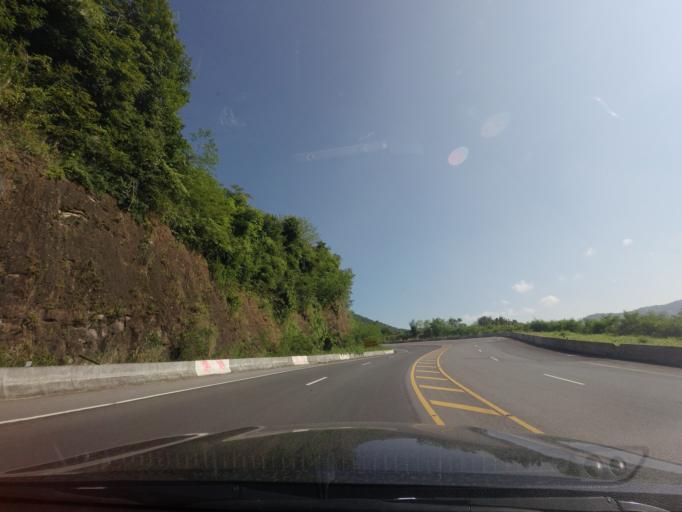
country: TH
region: Phetchabun
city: Lom Sak
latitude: 16.7806
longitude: 101.0981
